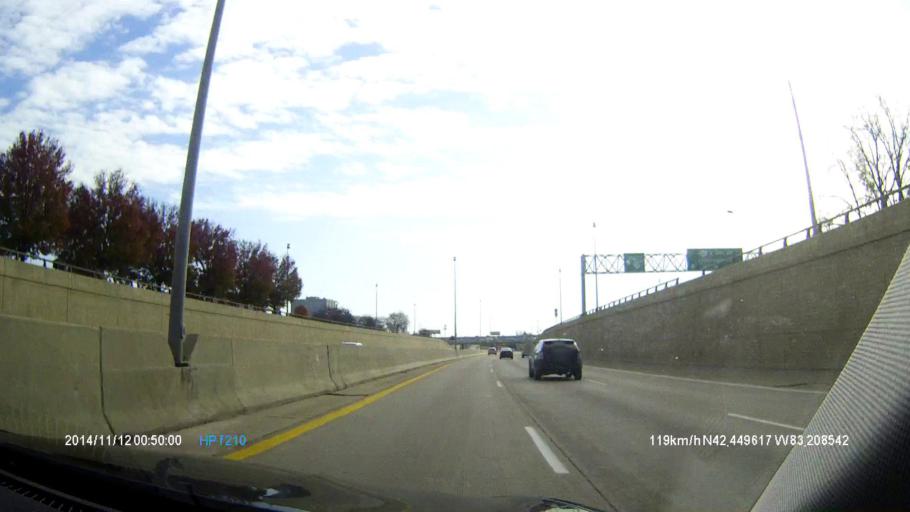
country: US
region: Michigan
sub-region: Oakland County
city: Oak Park
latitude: 42.4494
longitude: -83.2083
